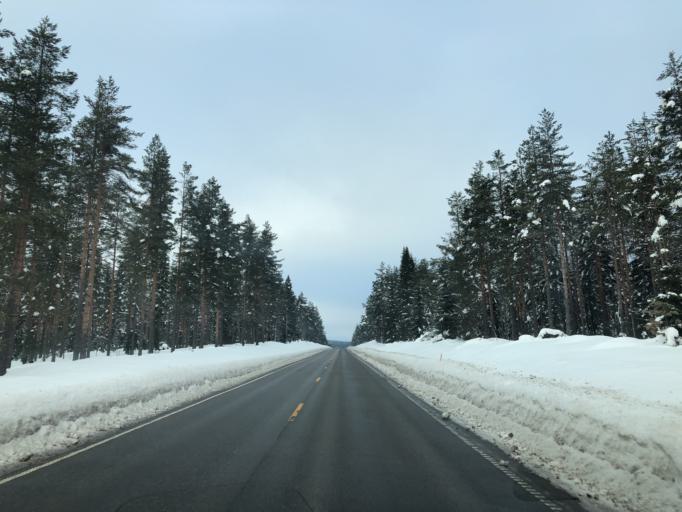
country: NO
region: Hedmark
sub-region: Trysil
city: Innbygda
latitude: 61.2067
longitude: 12.2228
